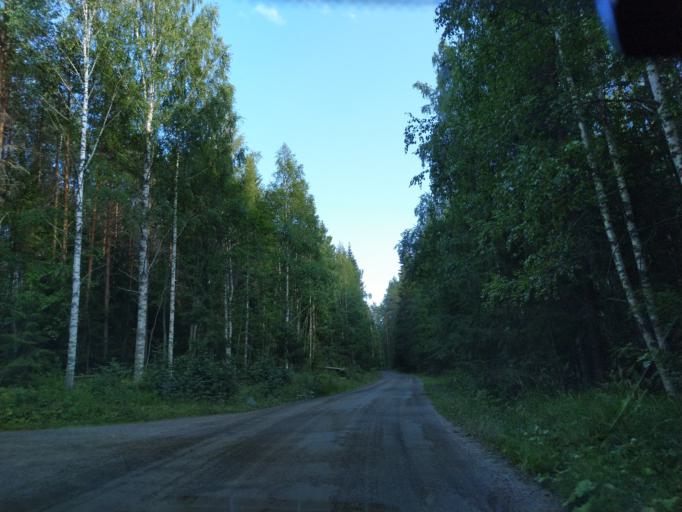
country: FI
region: Central Finland
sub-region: Jaemsae
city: Kuhmoinen
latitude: 61.6889
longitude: 24.9623
